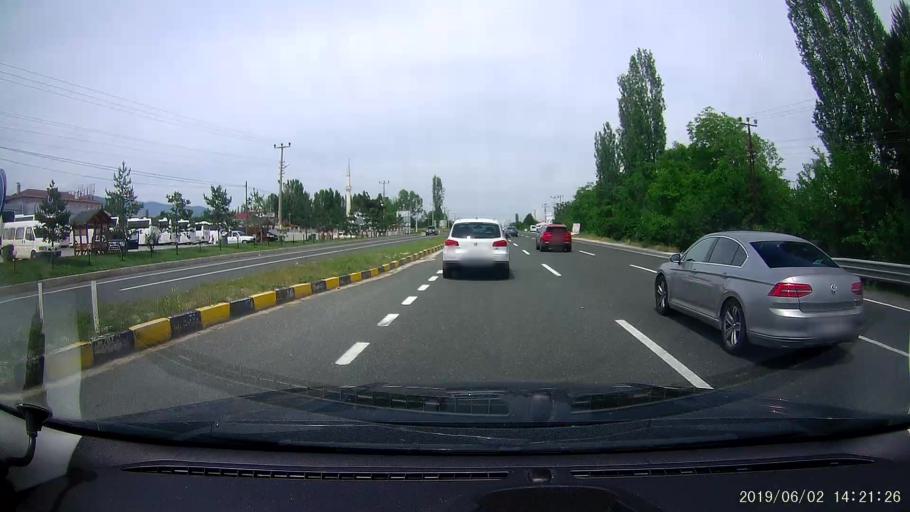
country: TR
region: Kastamonu
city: Tosya
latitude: 40.9785
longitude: 34.0021
